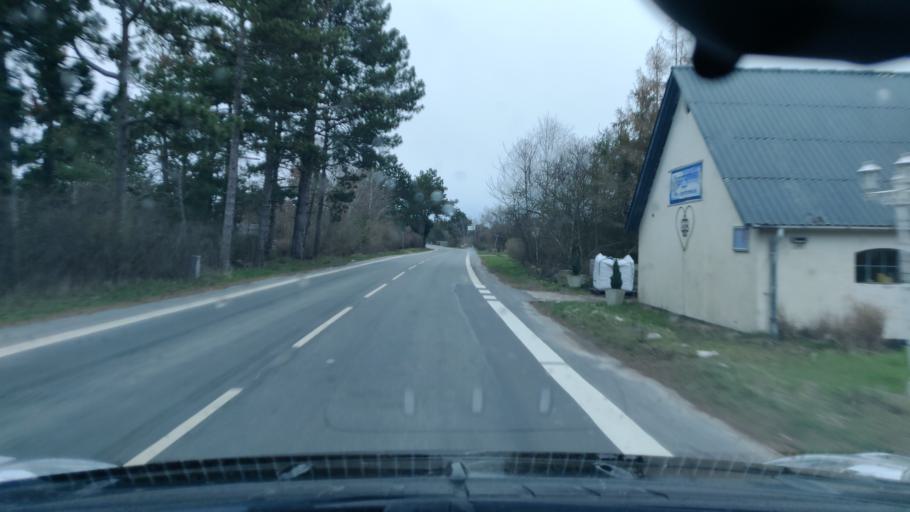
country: DK
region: Zealand
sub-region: Odsherred Kommune
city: Asnaes
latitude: 55.8679
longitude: 11.5368
